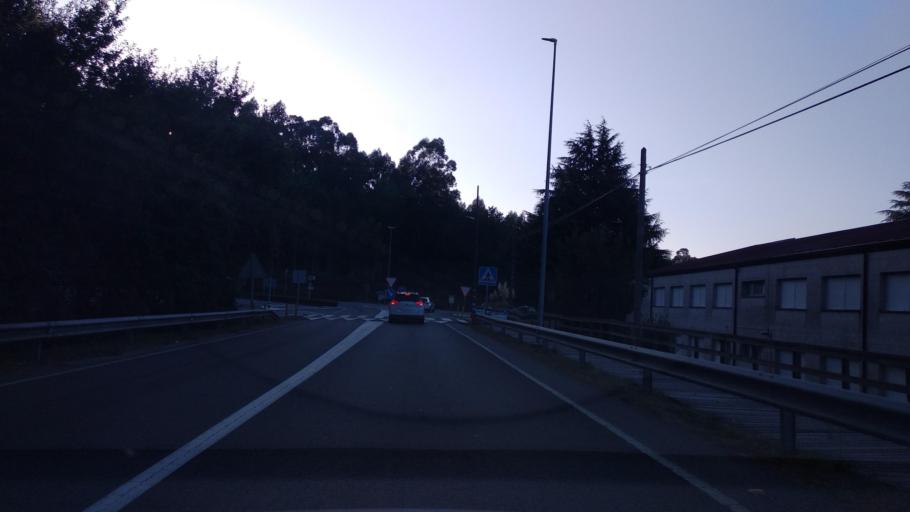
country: ES
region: Galicia
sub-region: Provincia de Pontevedra
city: Redondela
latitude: 42.3365
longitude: -8.5858
